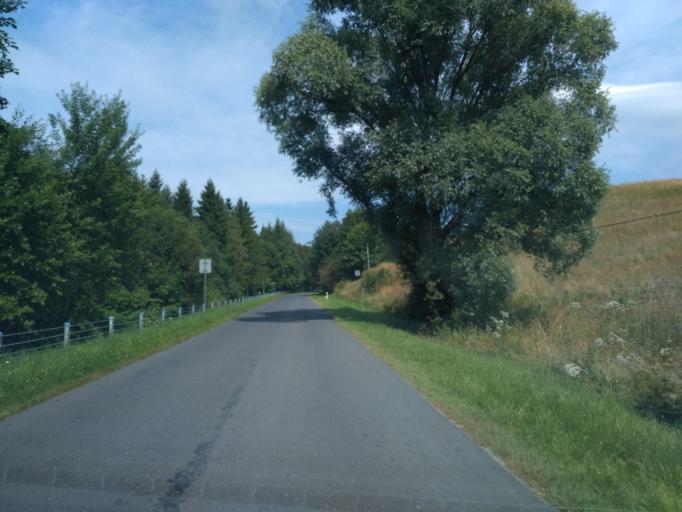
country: PL
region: Subcarpathian Voivodeship
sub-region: Powiat leski
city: Polanczyk
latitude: 49.3091
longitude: 22.5242
